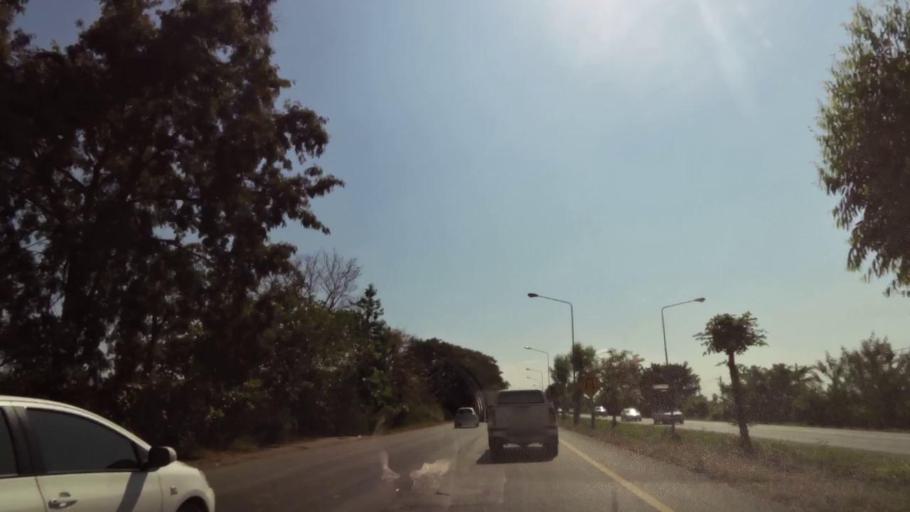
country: TH
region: Nakhon Sawan
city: Kao Liao
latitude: 15.8009
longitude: 100.1203
